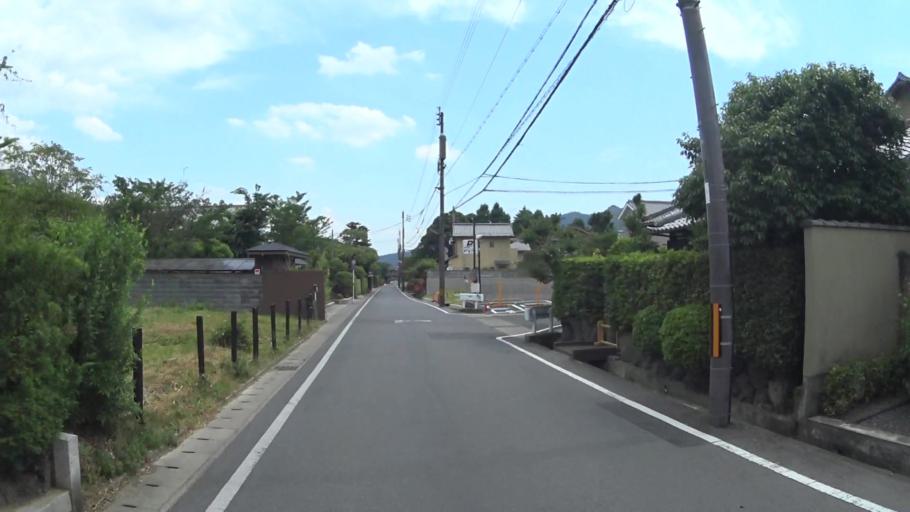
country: JP
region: Kyoto
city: Muko
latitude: 35.0259
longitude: 135.6784
